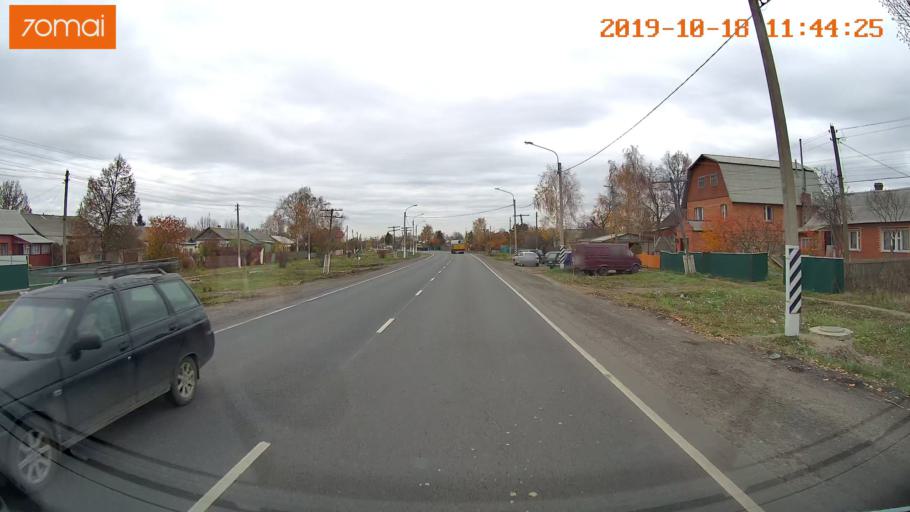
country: RU
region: Rjazan
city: Oktyabr'skiy
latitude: 54.2023
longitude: 38.9572
